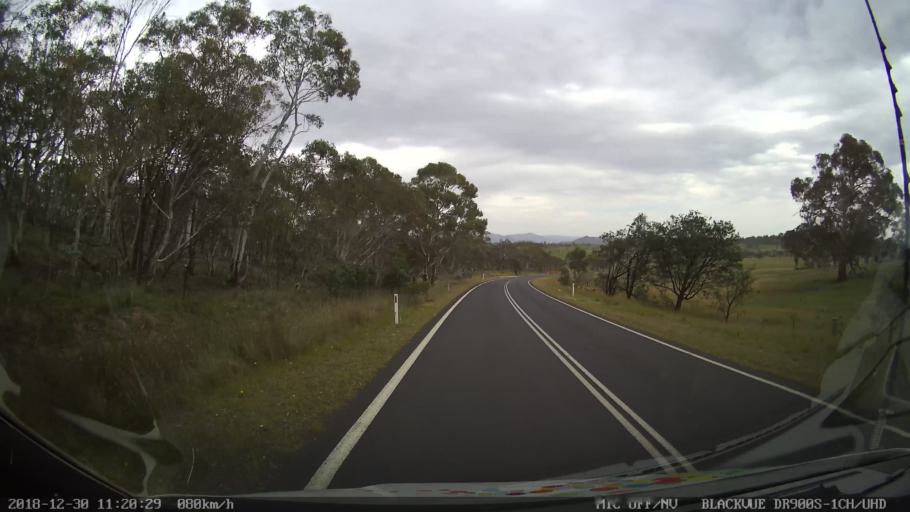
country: AU
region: New South Wales
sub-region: Snowy River
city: Jindabyne
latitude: -36.5177
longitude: 148.6888
